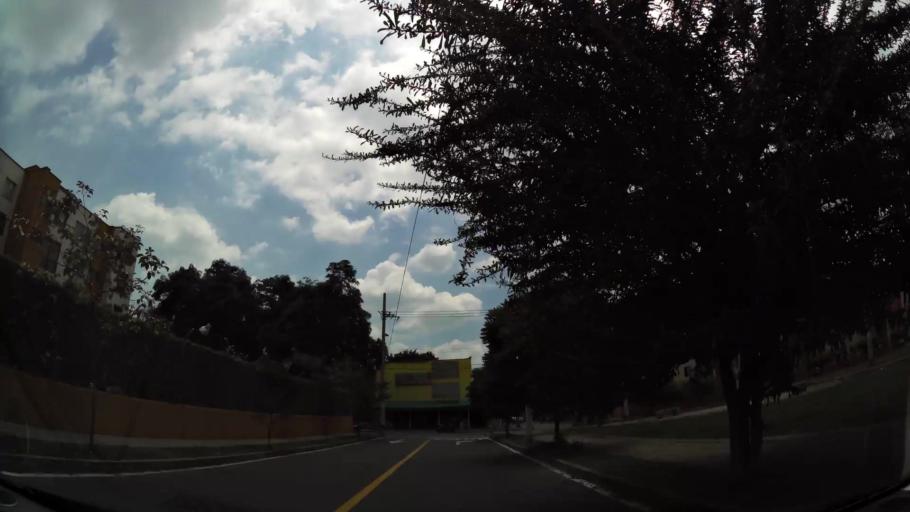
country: CO
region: Valle del Cauca
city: Cali
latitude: 3.4794
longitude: -76.4982
